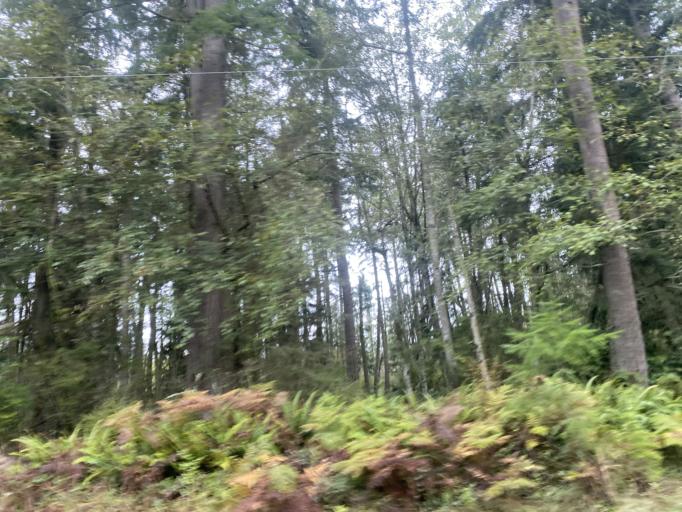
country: US
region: Washington
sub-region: Island County
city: Freeland
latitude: 48.0775
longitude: -122.5612
